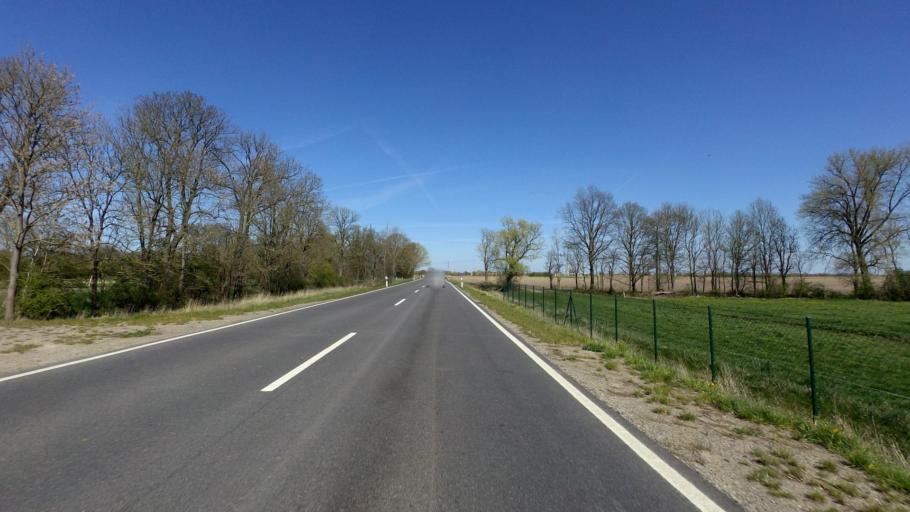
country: DE
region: Saxony-Anhalt
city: Kalbe
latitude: 52.6504
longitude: 11.3564
